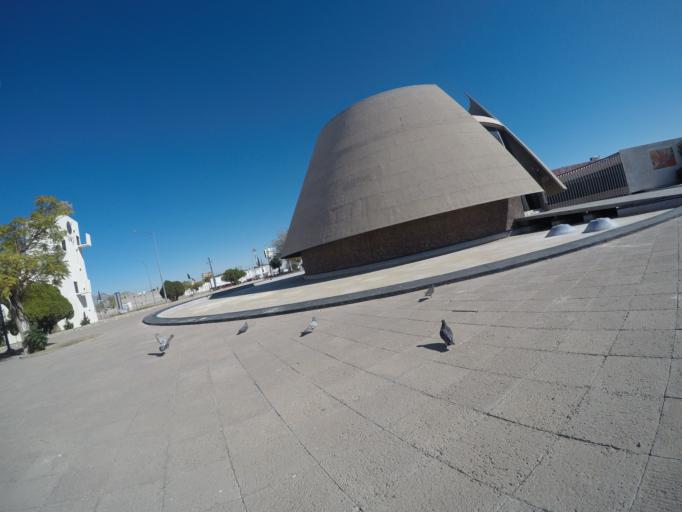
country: MX
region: Chihuahua
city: Ciudad Juarez
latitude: 31.7410
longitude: -106.4547
